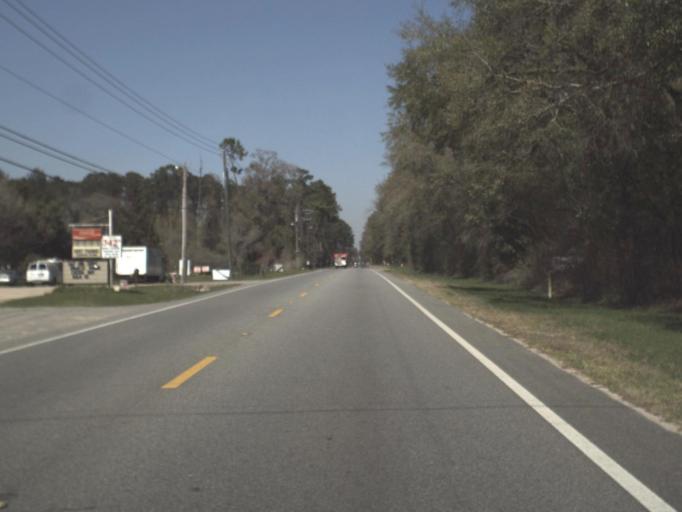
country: US
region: Florida
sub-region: Leon County
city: Woodville
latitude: 30.2938
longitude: -84.2431
